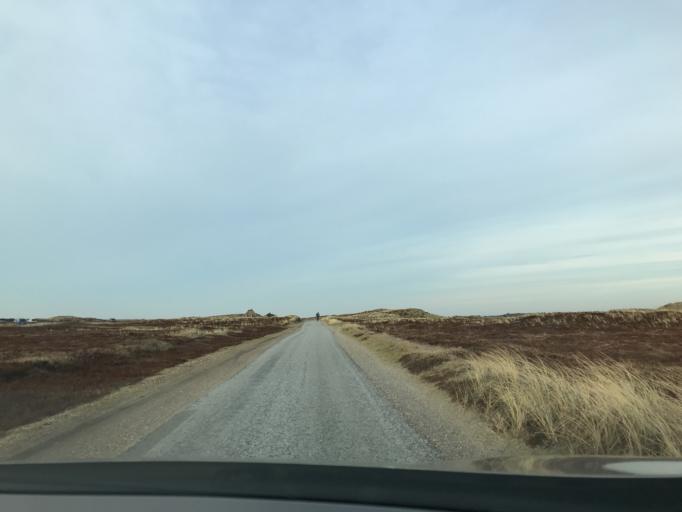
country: DK
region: Central Jutland
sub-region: Ringkobing-Skjern Kommune
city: Hvide Sande
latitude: 55.8150
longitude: 8.1767
